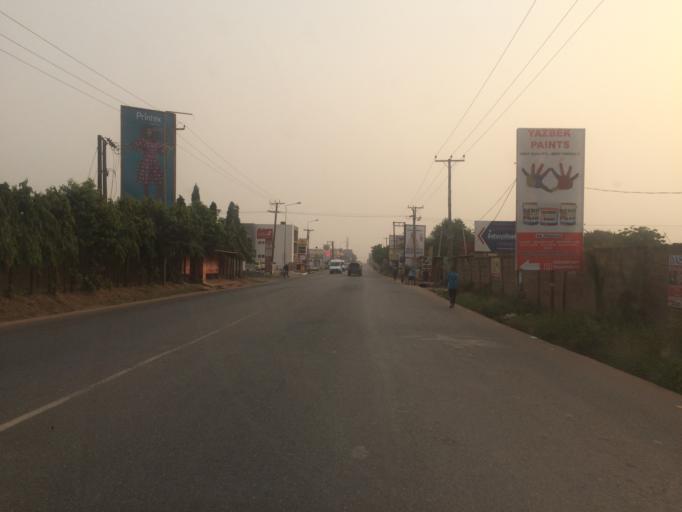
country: GH
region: Greater Accra
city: Medina Estates
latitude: 5.6402
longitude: -0.1202
